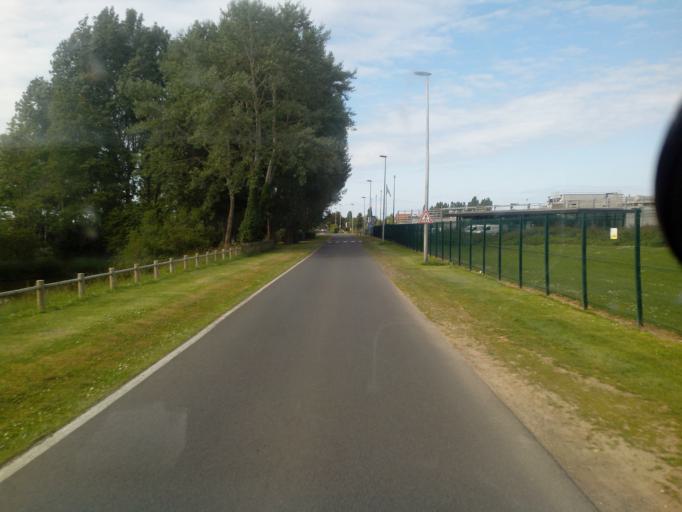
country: FR
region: Lower Normandy
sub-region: Departement du Calvados
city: Cabourg
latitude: 49.2773
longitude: -0.1164
